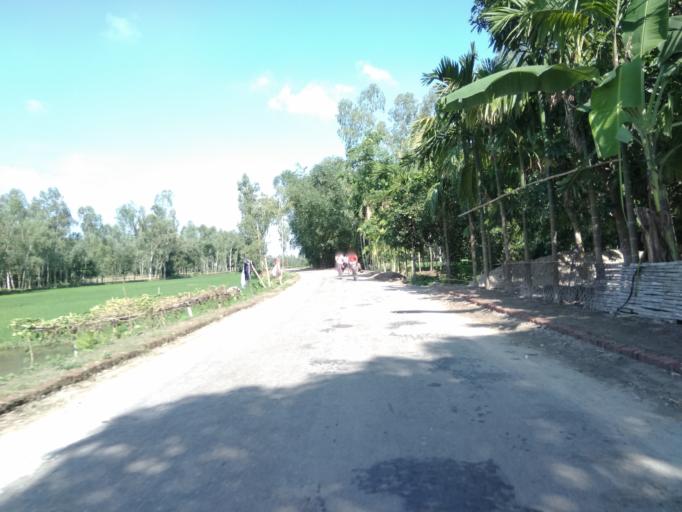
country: BD
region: Rangpur Division
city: Panchagarh
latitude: 26.2556
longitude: 88.6162
